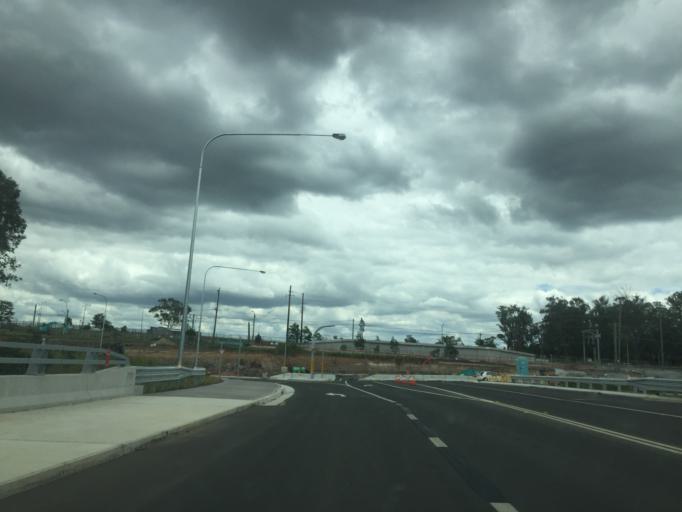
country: AU
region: New South Wales
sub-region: Blacktown
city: Riverstone
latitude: -33.7013
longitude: 150.8743
